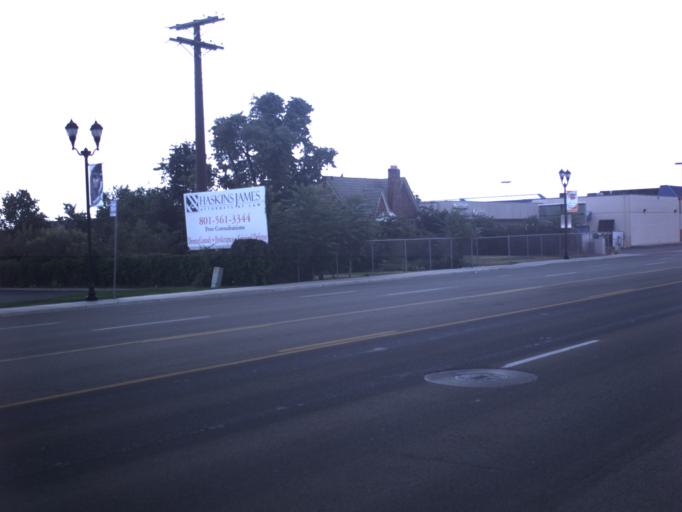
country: US
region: Utah
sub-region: Salt Lake County
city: Midvale
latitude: 40.6186
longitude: -111.8905
